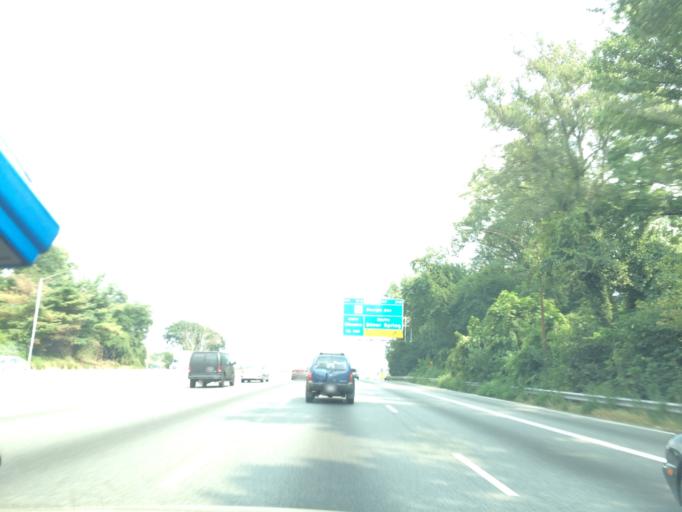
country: US
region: Maryland
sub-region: Montgomery County
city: Forest Glen
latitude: 39.0135
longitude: -77.0459
